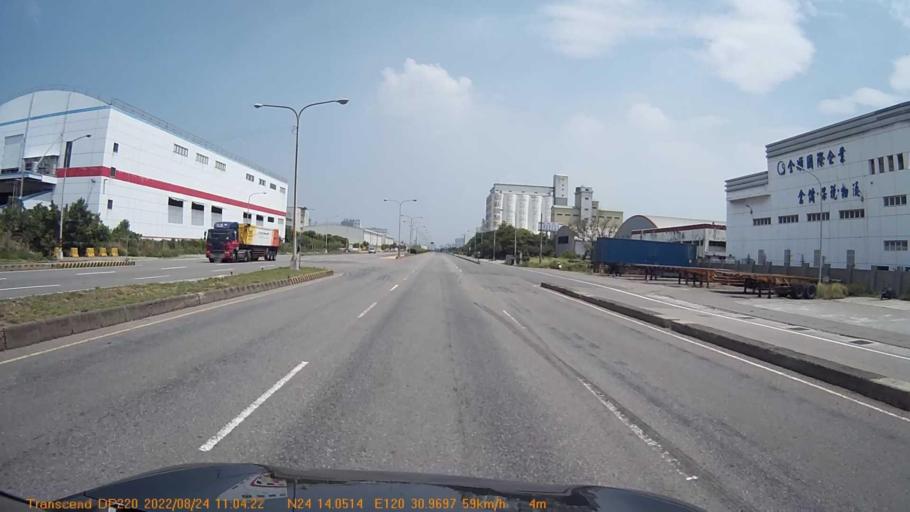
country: TW
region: Taiwan
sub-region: Changhua
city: Chang-hua
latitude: 24.2347
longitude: 120.5164
